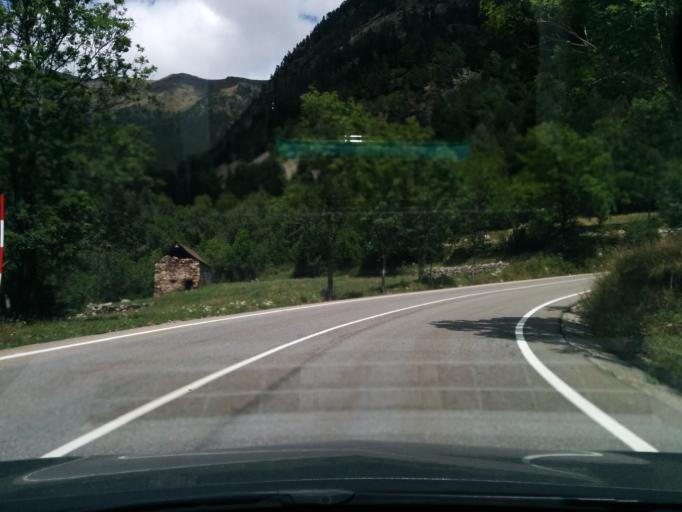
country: ES
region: Aragon
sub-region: Provincia de Huesca
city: Bielsa
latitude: 42.7040
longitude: 0.1997
